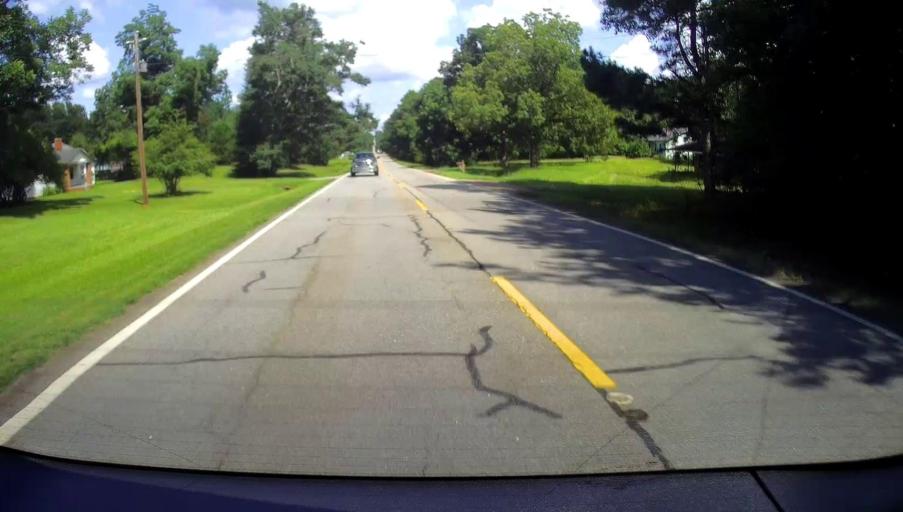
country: US
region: Georgia
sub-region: Upson County
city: Thomaston
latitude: 32.9218
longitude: -84.2225
